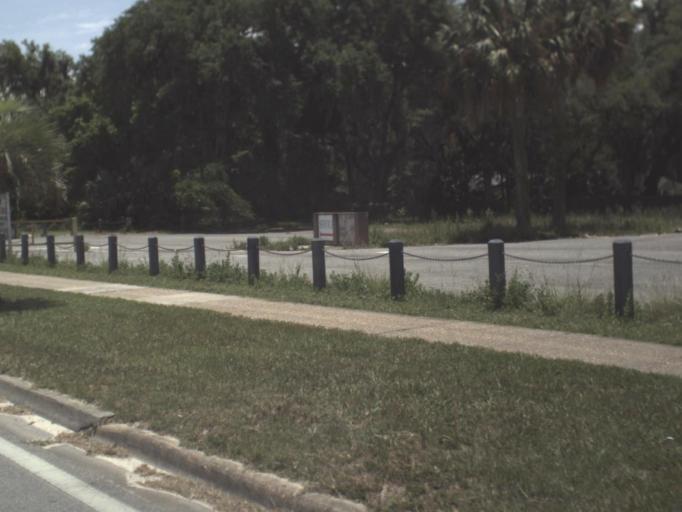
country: US
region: Florida
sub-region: Dixie County
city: Cross City
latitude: 29.6357
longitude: -83.1271
